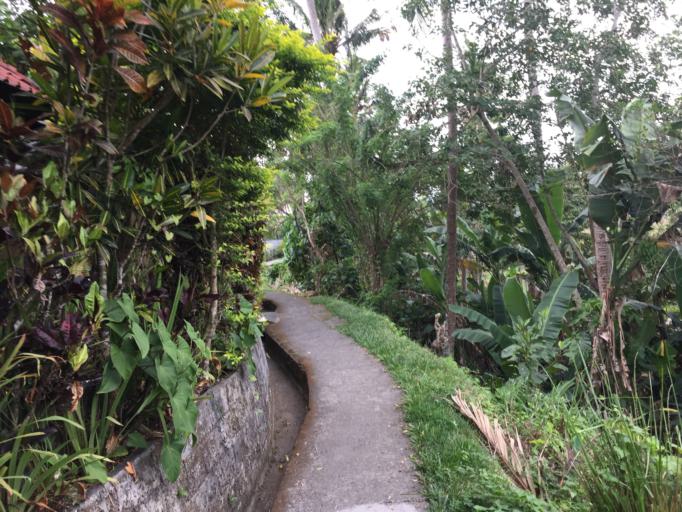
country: ID
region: Bali
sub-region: Kabupaten Gianyar
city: Ubud
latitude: -8.5014
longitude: 115.2517
